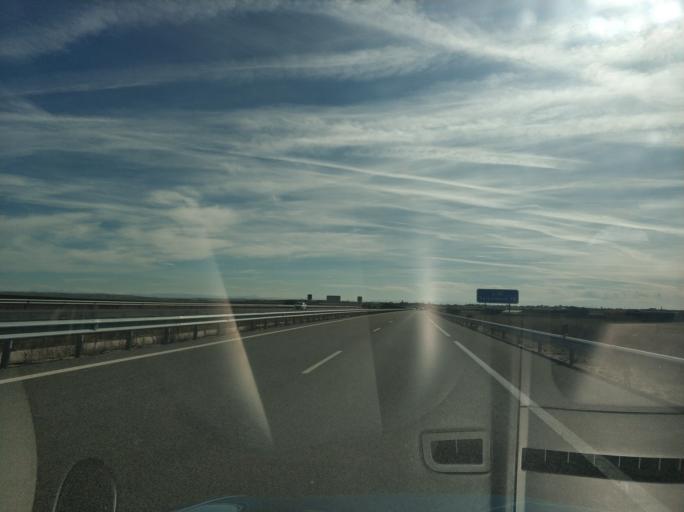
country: ES
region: Castille and Leon
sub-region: Provincia de Salamanca
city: Calzada de Valdunciel
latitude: 41.0778
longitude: -5.6877
